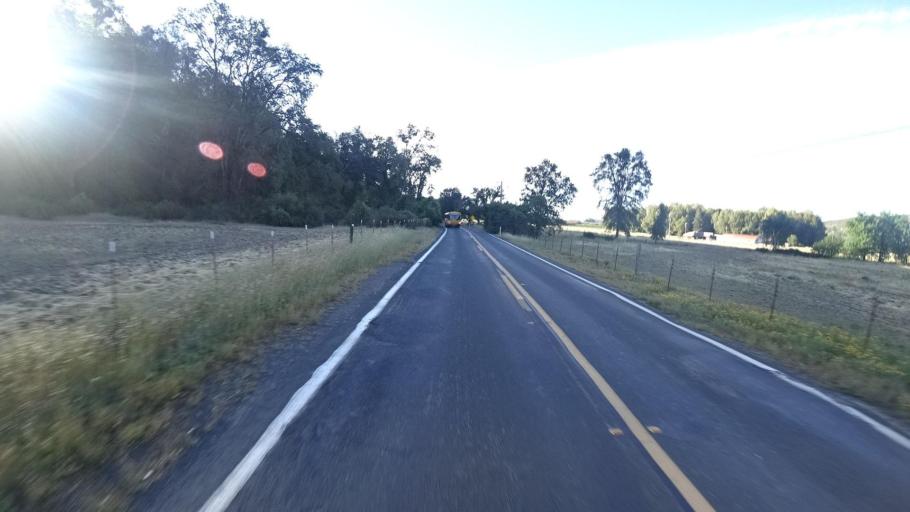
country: US
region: California
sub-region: Lake County
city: Upper Lake
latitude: 39.2038
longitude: -122.9052
